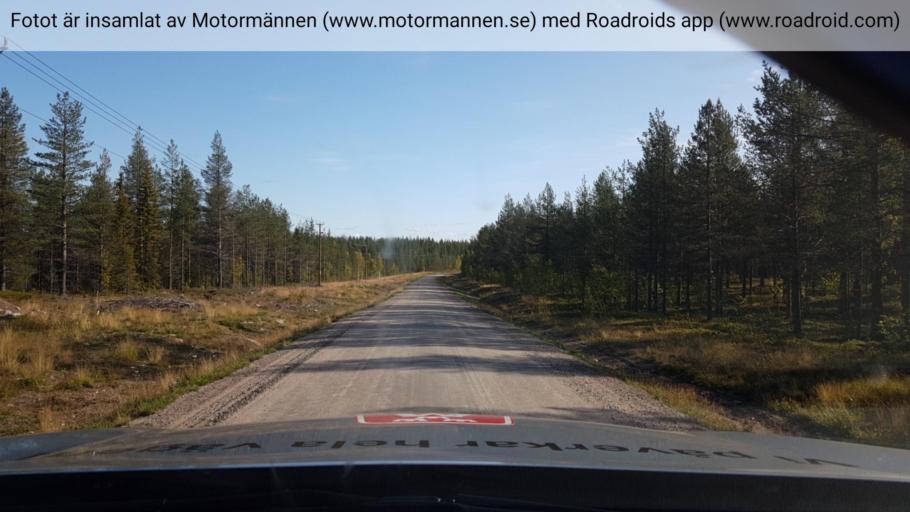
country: SE
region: Norrbotten
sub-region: Pajala Kommun
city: Pajala
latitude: 67.7244
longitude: 22.1638
